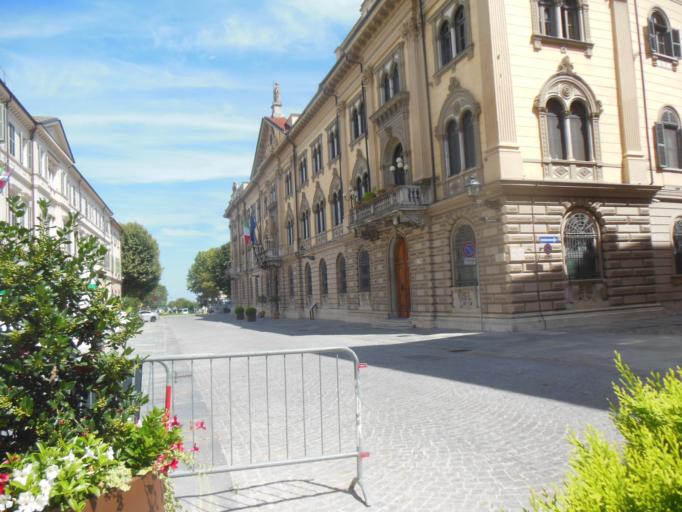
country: IT
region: Piedmont
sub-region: Provincia di Cuneo
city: Cuneo
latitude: 44.3944
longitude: 7.5531
